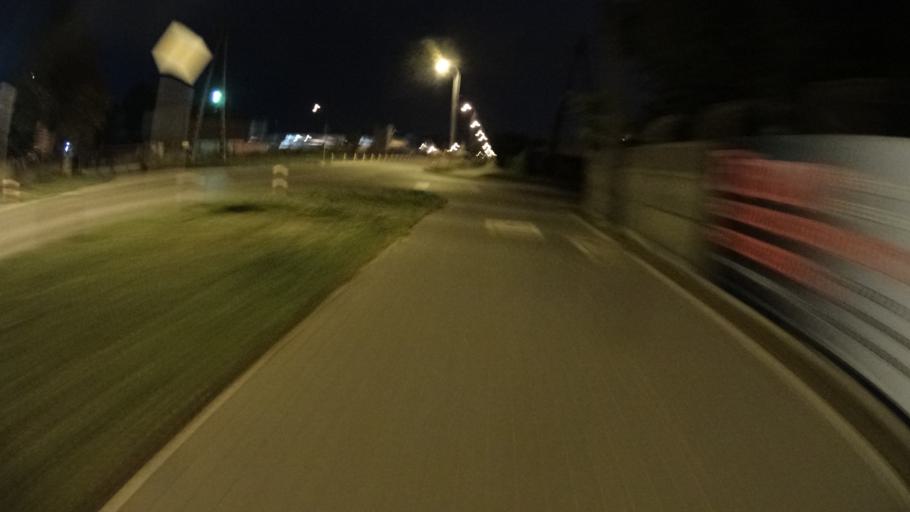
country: PL
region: Masovian Voivodeship
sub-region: Powiat pruszkowski
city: Otrebusy
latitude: 52.1604
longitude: 20.7661
